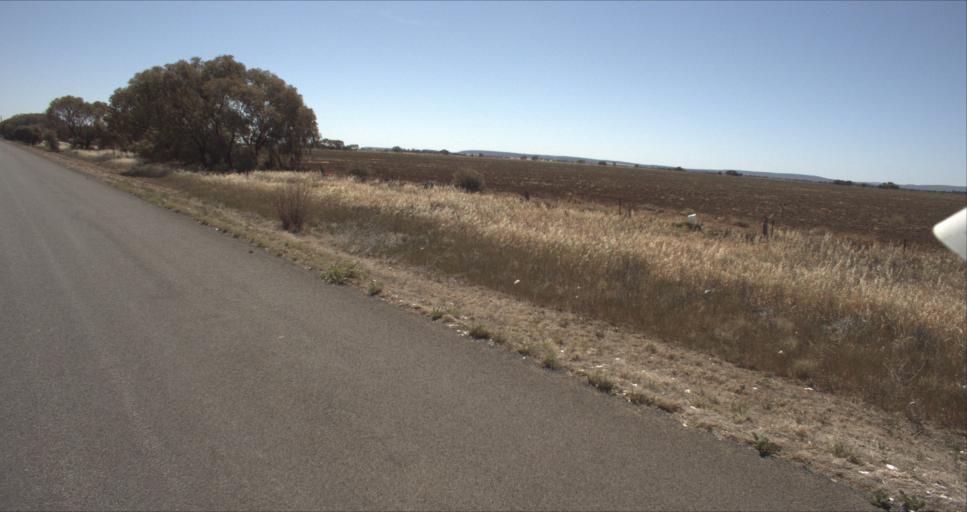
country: AU
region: New South Wales
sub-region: Leeton
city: Leeton
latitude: -34.4779
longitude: 146.2911
